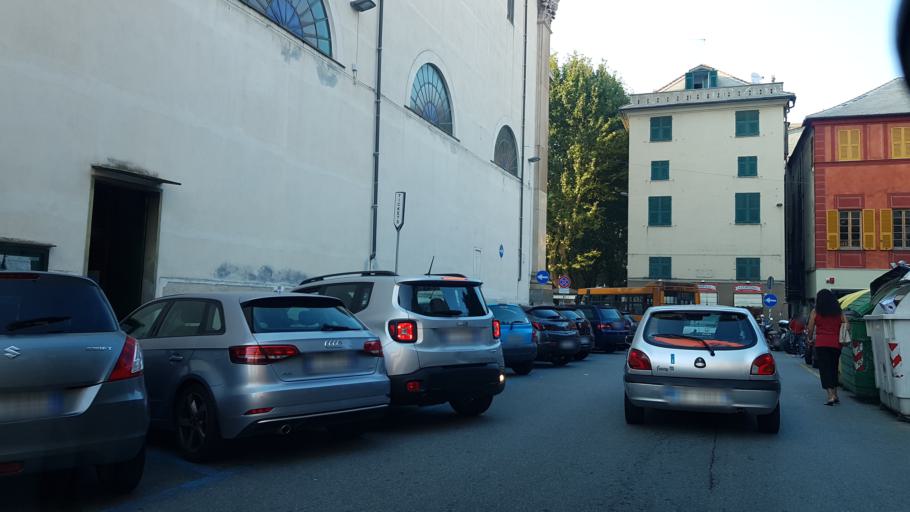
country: IT
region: Liguria
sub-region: Provincia di Genova
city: San Teodoro
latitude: 44.4244
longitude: 8.8493
